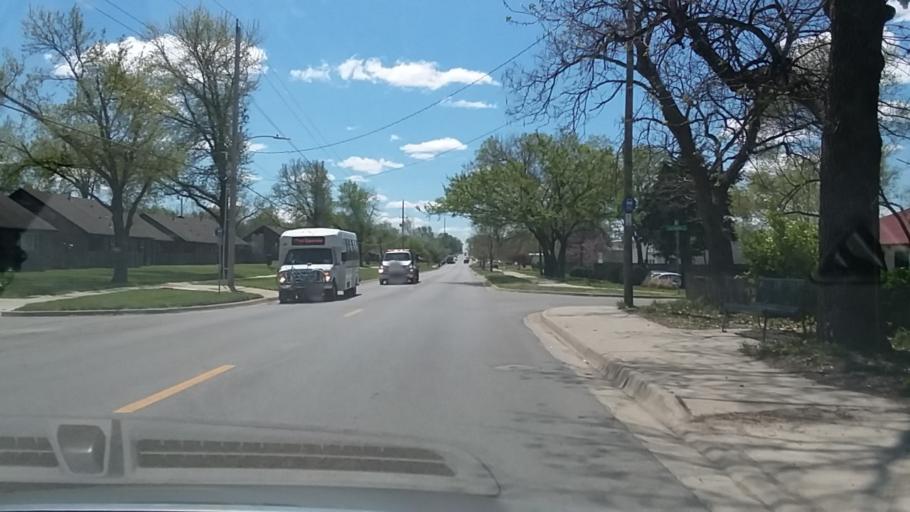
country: US
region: Kansas
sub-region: Douglas County
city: Lawrence
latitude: 38.9538
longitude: -95.2235
